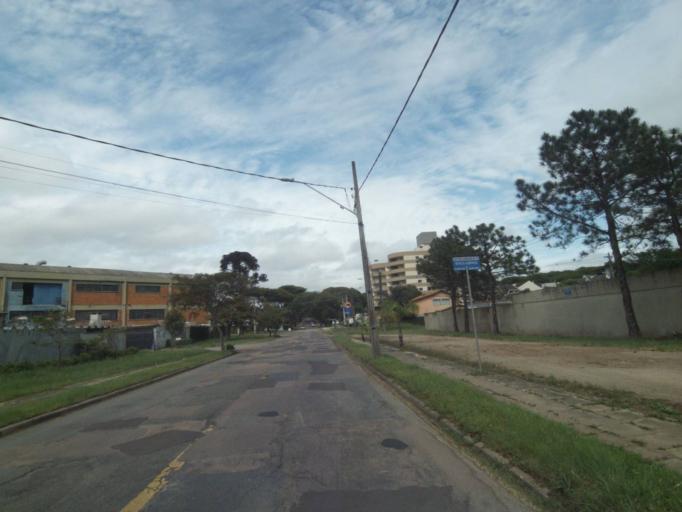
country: BR
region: Parana
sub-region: Pinhais
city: Pinhais
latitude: -25.4222
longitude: -49.2266
